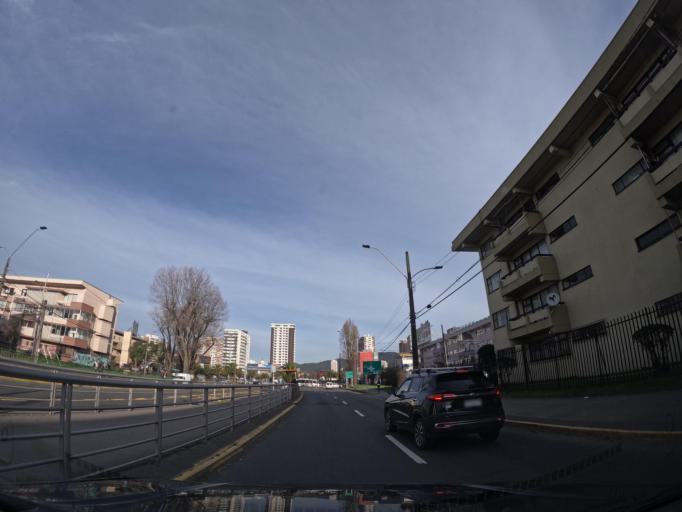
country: CL
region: Biobio
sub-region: Provincia de Concepcion
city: Concepcion
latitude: -36.8189
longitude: -73.0451
